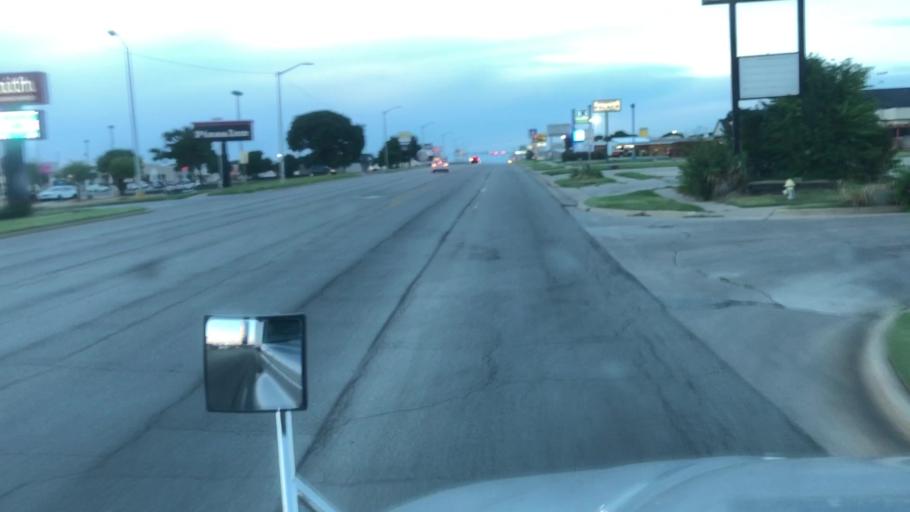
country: US
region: Oklahoma
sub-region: Kay County
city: Ponca City
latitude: 36.7341
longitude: -97.0672
